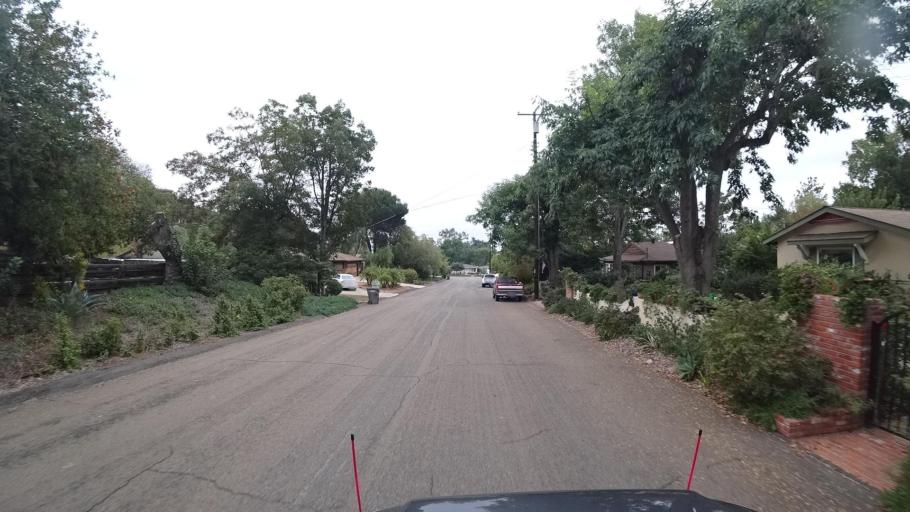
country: US
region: California
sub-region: San Diego County
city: Casa de Oro-Mount Helix
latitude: 32.7600
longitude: -116.9745
